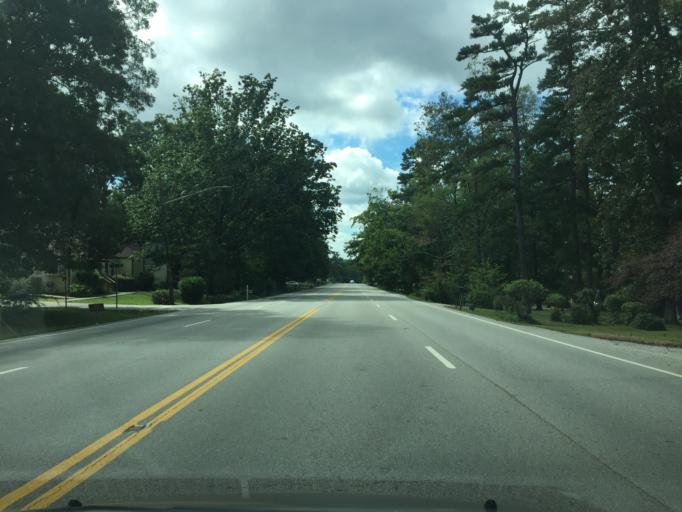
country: US
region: Tennessee
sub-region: Hamilton County
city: Signal Mountain
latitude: 35.1245
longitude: -85.3385
